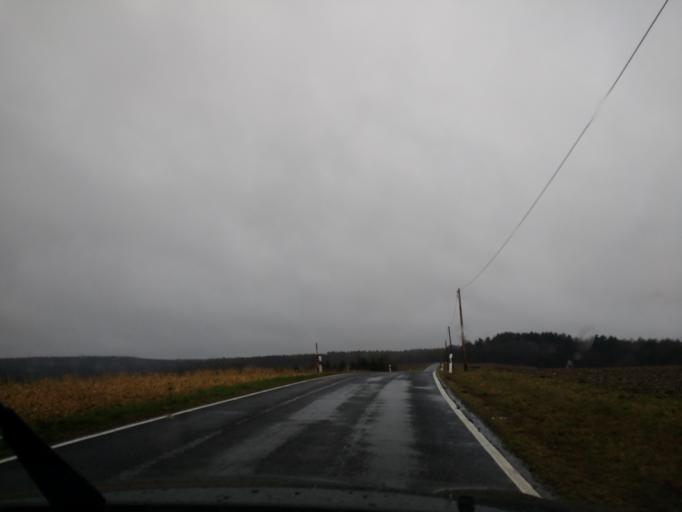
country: DE
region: Rheinland-Pfalz
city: Geisfeld
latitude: 49.6955
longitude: 6.9479
